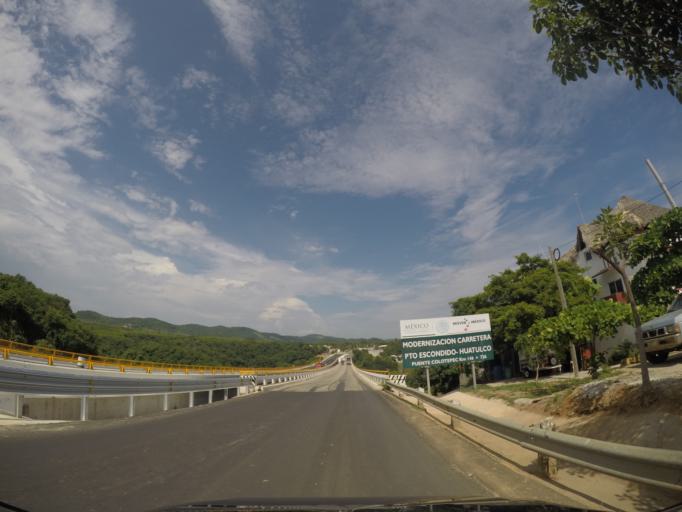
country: MX
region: Oaxaca
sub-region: Santa Maria Colotepec
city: Brisas de Zicatela
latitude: 15.8270
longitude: -97.0280
